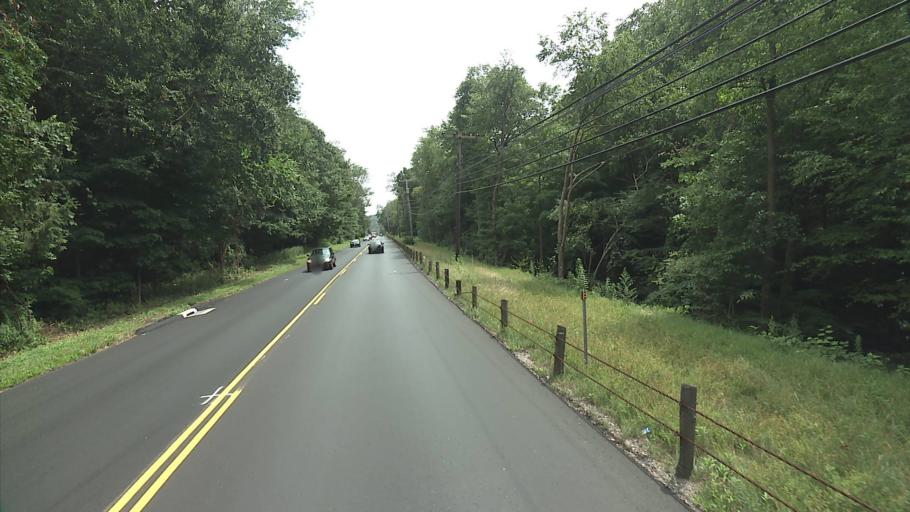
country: US
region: Connecticut
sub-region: New Haven County
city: Oxford
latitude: 41.4157
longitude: -73.1002
